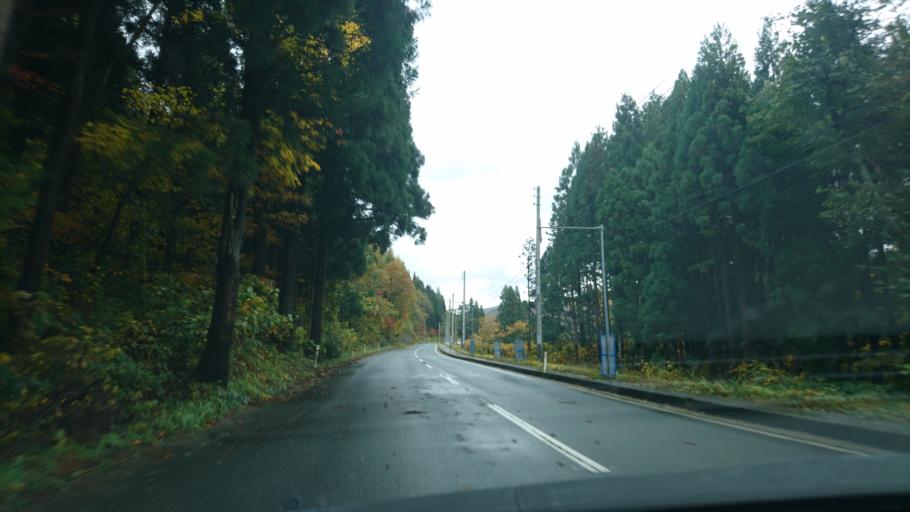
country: JP
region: Iwate
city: Shizukuishi
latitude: 39.5017
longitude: 140.8186
